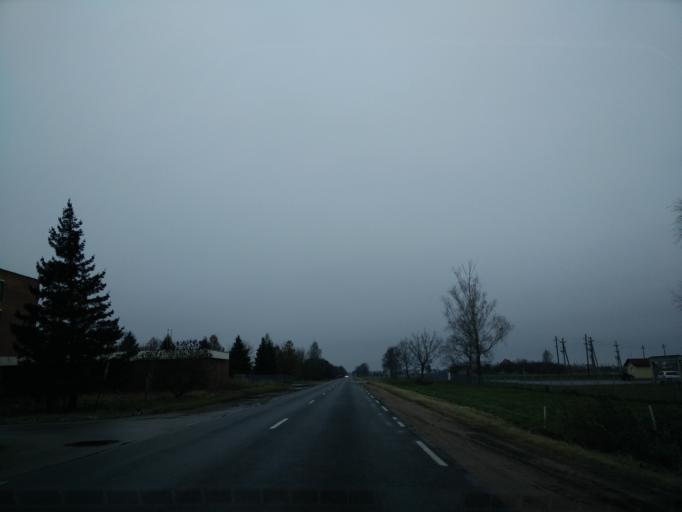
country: LT
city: Ariogala
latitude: 55.2589
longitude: 23.4963
